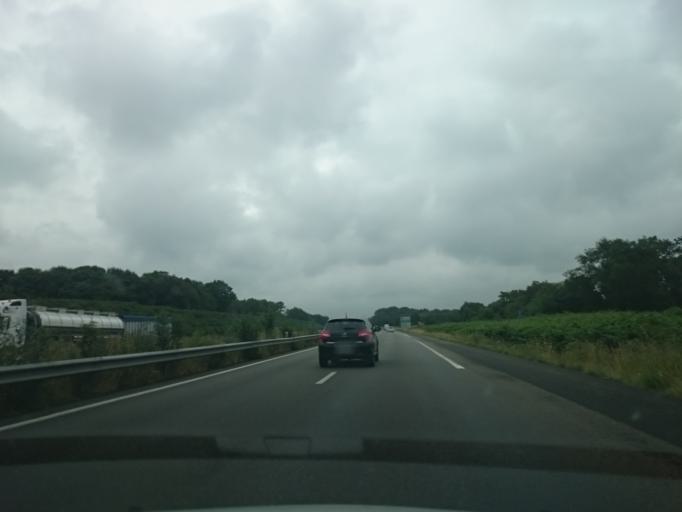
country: FR
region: Pays de la Loire
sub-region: Departement de la Loire-Atlantique
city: Sautron
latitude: 47.2607
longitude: -1.6999
